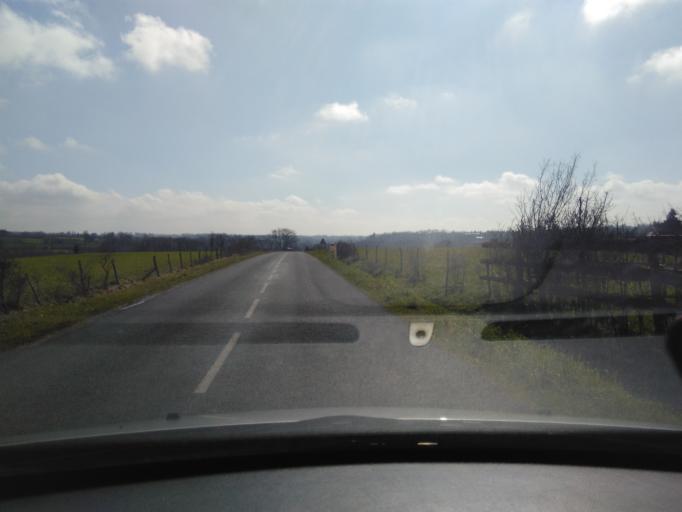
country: FR
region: Pays de la Loire
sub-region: Departement de la Vendee
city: Sainte-Cecile
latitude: 46.7068
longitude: -1.1180
